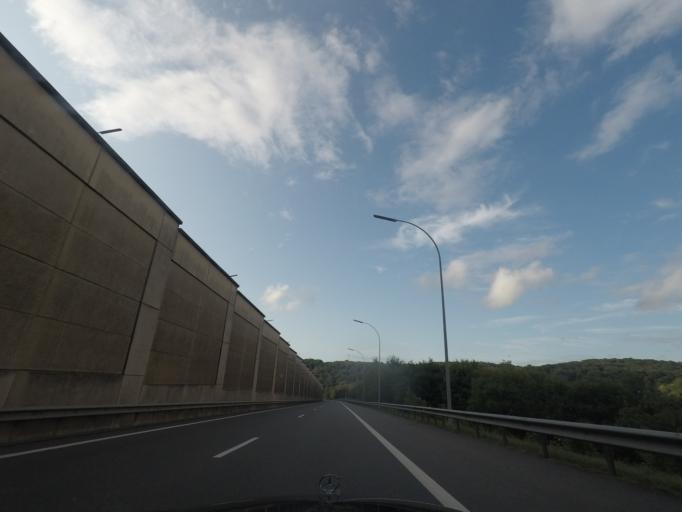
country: LU
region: Luxembourg
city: Colmar
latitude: 49.8061
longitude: 6.1095
